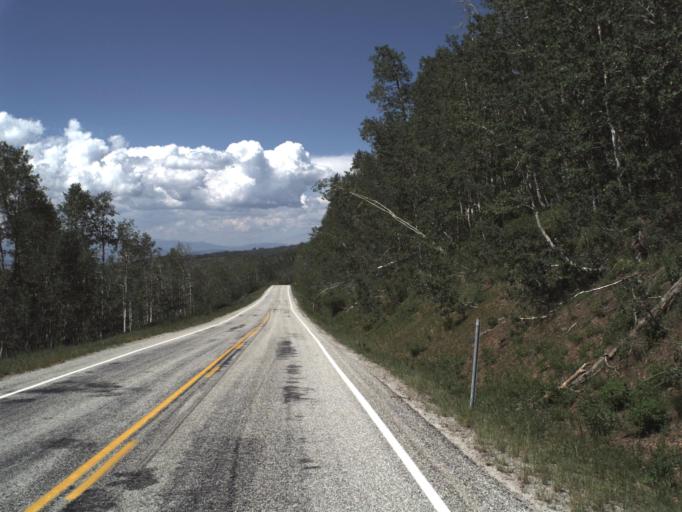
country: US
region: Utah
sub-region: Weber County
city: Wolf Creek
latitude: 41.4053
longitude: -111.5283
